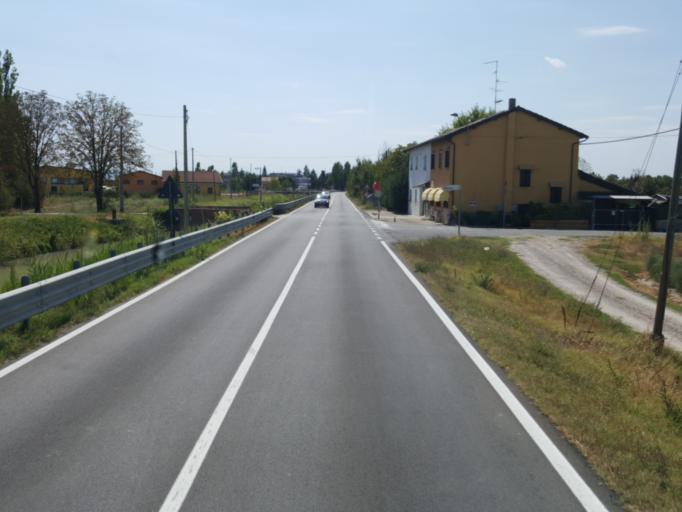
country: IT
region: Emilia-Romagna
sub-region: Provincia di Reggio Emilia
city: Novellara
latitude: 44.8606
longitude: 10.7474
